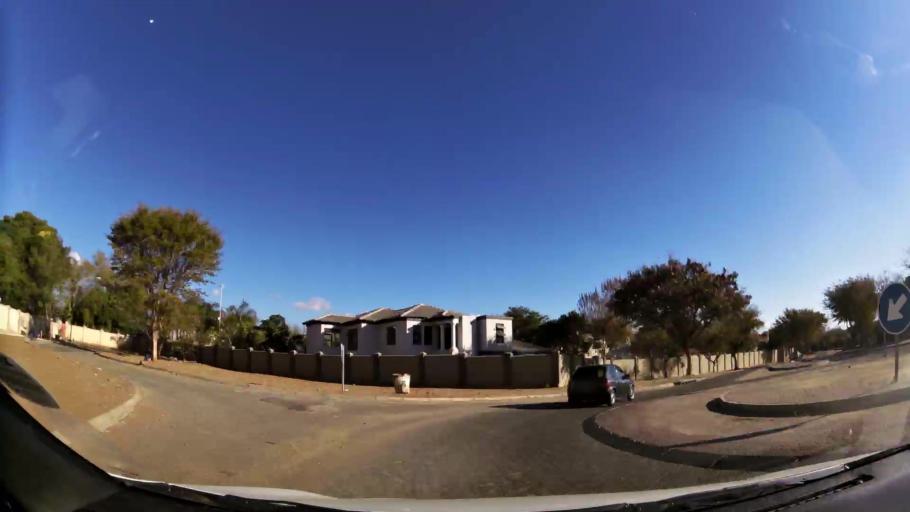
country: ZA
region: Limpopo
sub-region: Capricorn District Municipality
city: Polokwane
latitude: -23.8912
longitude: 29.4761
